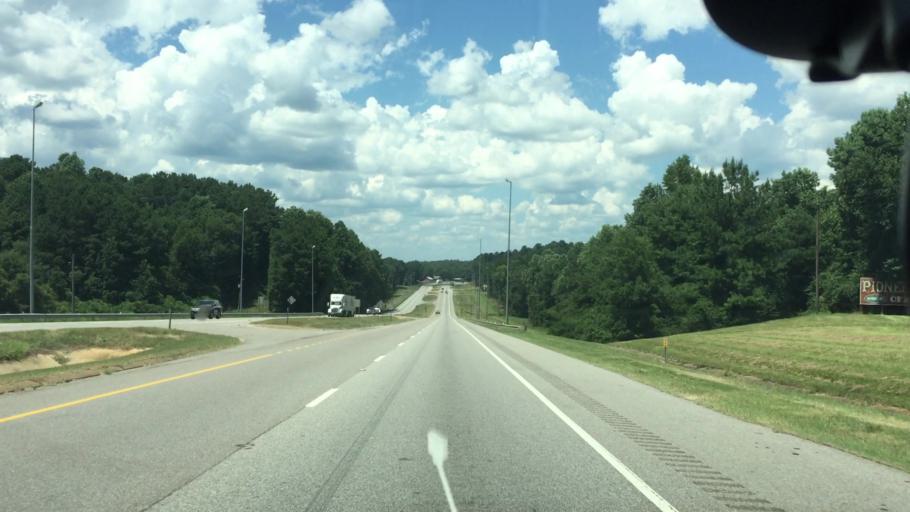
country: US
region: Alabama
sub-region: Pike County
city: Troy
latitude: 31.8142
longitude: -85.9918
